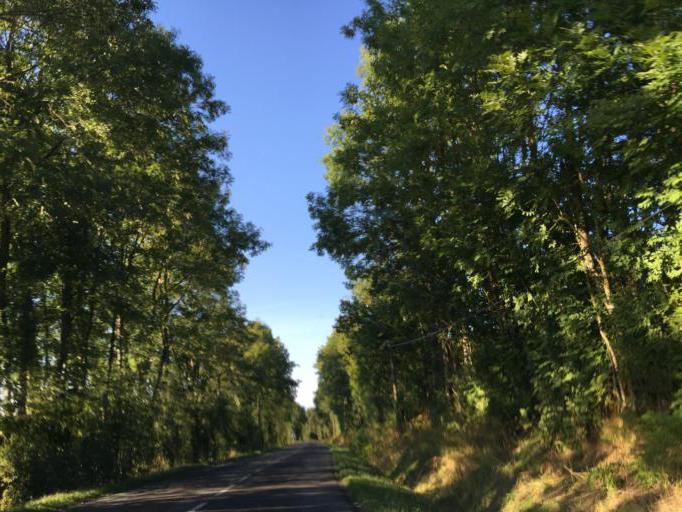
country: FR
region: Midi-Pyrenees
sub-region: Departement de l'Aveyron
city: Salles-Curan
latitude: 44.1442
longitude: 2.8634
